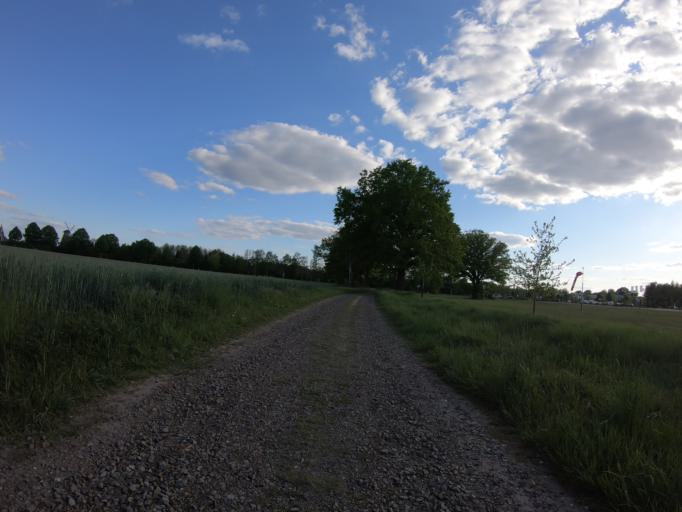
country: DE
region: Lower Saxony
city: Gifhorn
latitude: 52.4963
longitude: 10.5506
